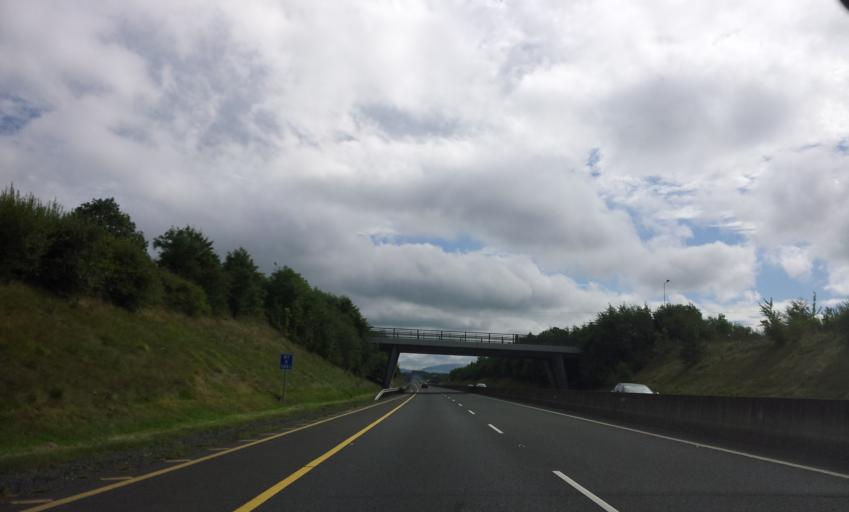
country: IE
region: Munster
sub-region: North Tipperary
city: Nenagh
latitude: 52.8449
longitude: -8.2097
